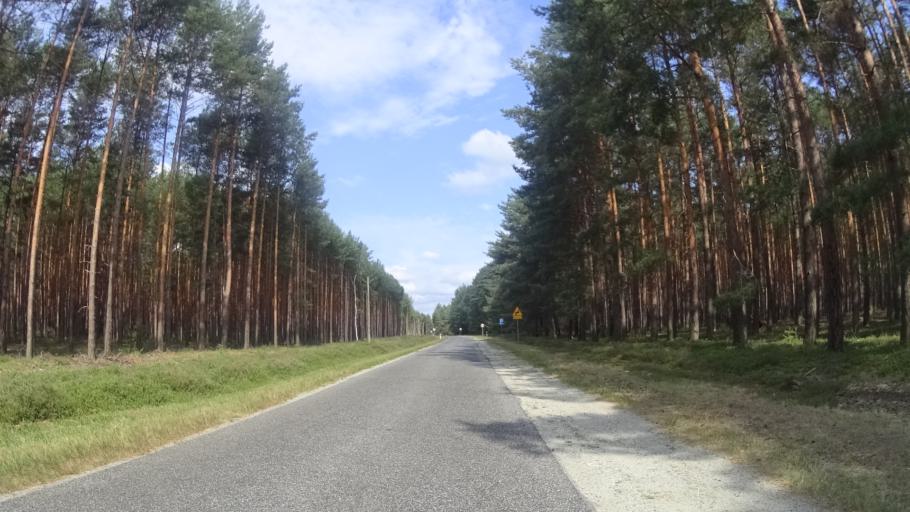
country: PL
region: Lubusz
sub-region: Powiat zarski
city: Leknica
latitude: 51.5207
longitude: 14.8260
